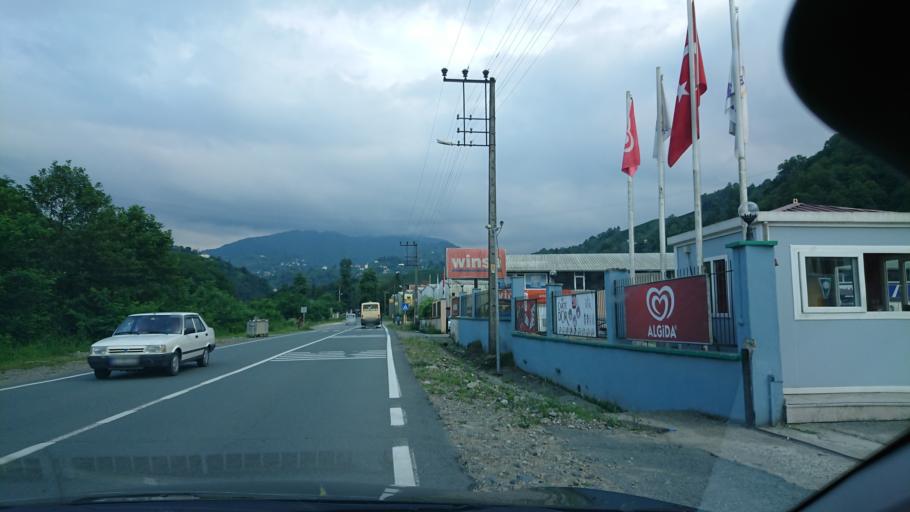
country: TR
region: Rize
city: Cayeli
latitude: 41.0644
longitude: 40.7158
